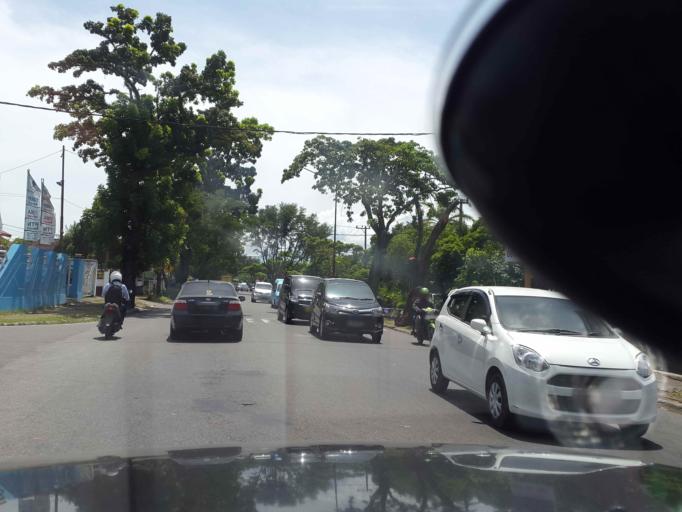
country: ID
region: West Sumatra
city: Padang
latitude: -0.9456
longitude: 100.3665
